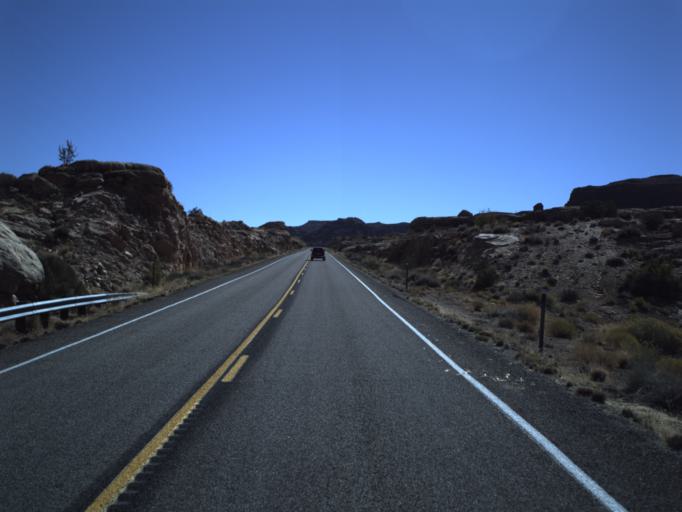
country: US
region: Utah
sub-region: San Juan County
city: Blanding
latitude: 37.8856
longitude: -110.3646
